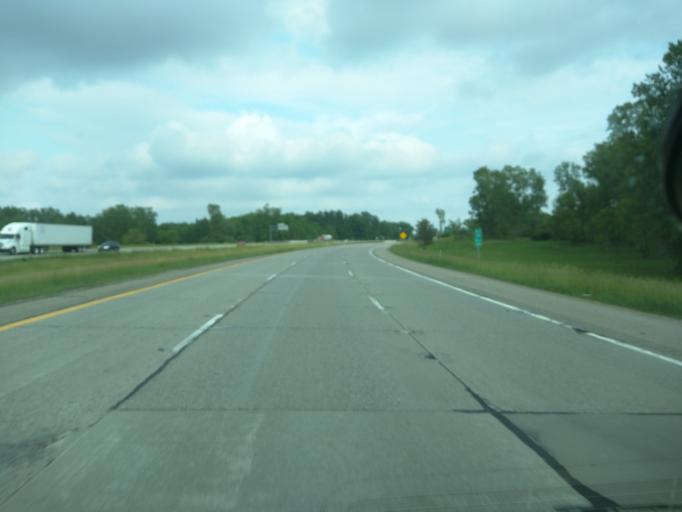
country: US
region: Michigan
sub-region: Clinton County
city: DeWitt
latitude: 42.8173
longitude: -84.5267
